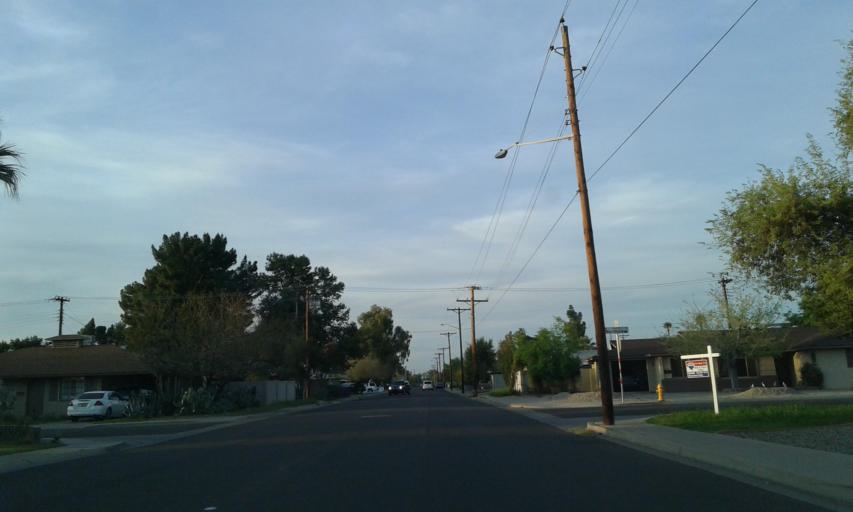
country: US
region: Arizona
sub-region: Maricopa County
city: Glendale
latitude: 33.5433
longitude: -112.1039
